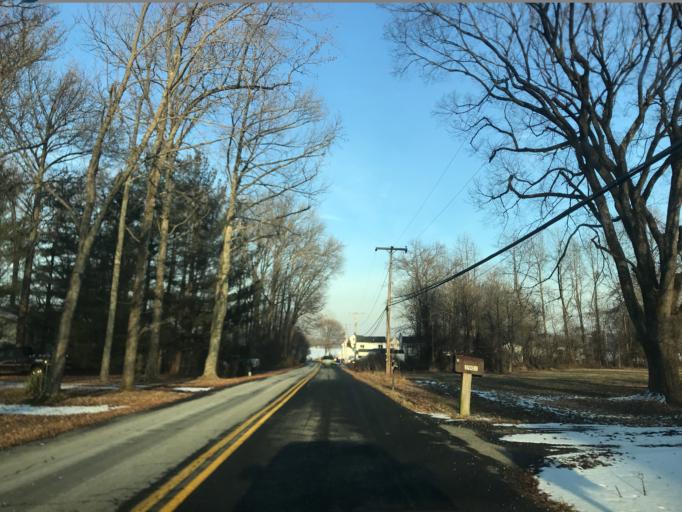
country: US
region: Maryland
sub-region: Harford County
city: Riverside
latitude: 39.4361
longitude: -76.2525
